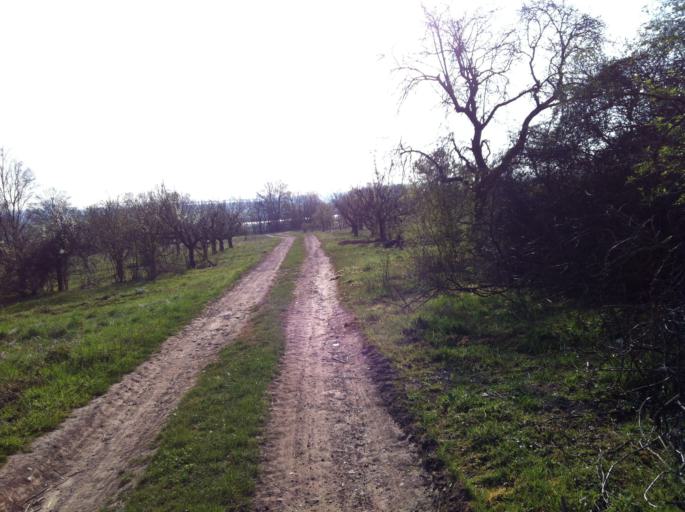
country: DE
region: Rheinland-Pfalz
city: Klein-Winternheim
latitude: 49.9842
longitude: 8.2015
